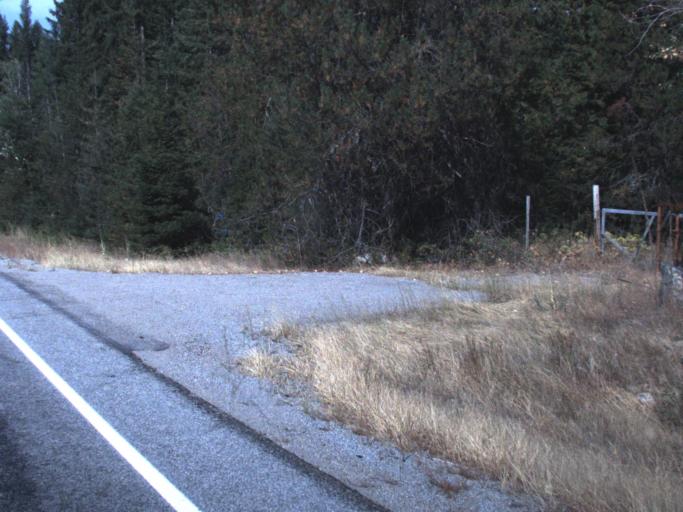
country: US
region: Washington
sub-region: Pend Oreille County
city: Newport
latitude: 48.2646
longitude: -117.2845
